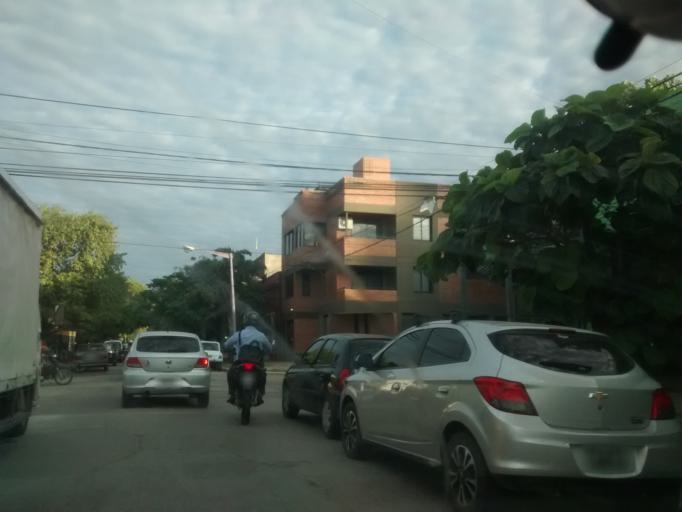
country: AR
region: Chaco
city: Resistencia
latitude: -27.4600
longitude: -58.9800
